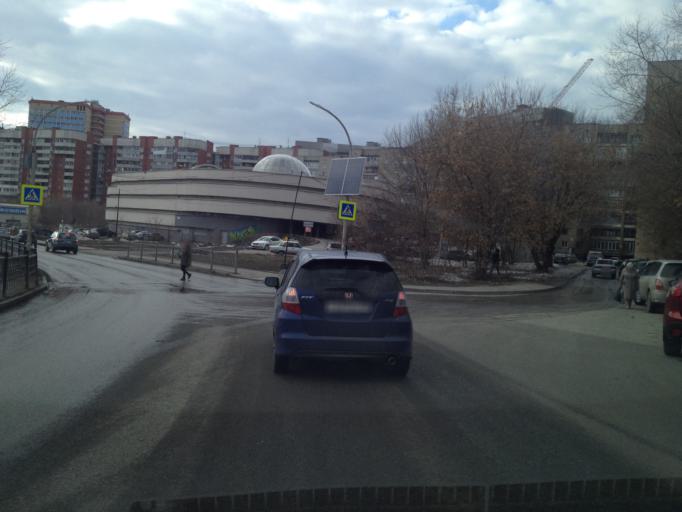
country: RU
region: Sverdlovsk
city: Yekaterinburg
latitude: 56.8527
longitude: 60.5793
